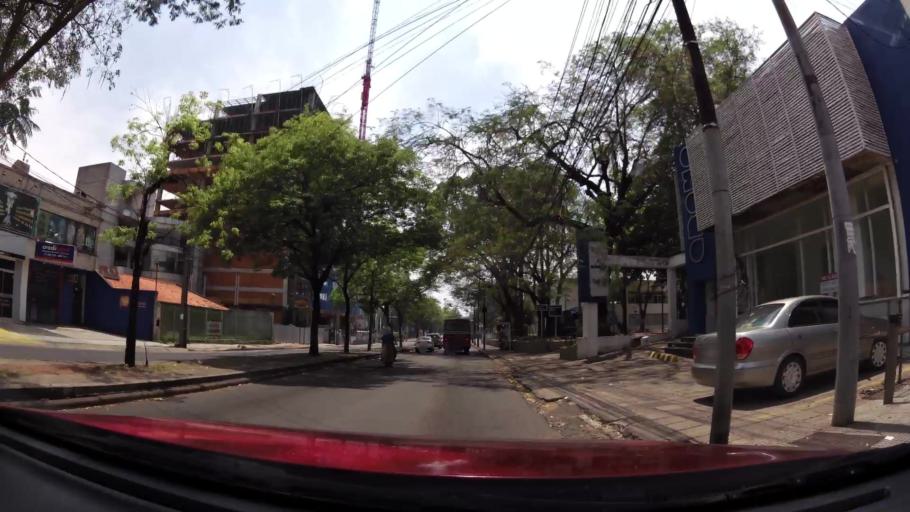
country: PY
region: Central
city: Lambare
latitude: -25.2963
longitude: -57.5777
